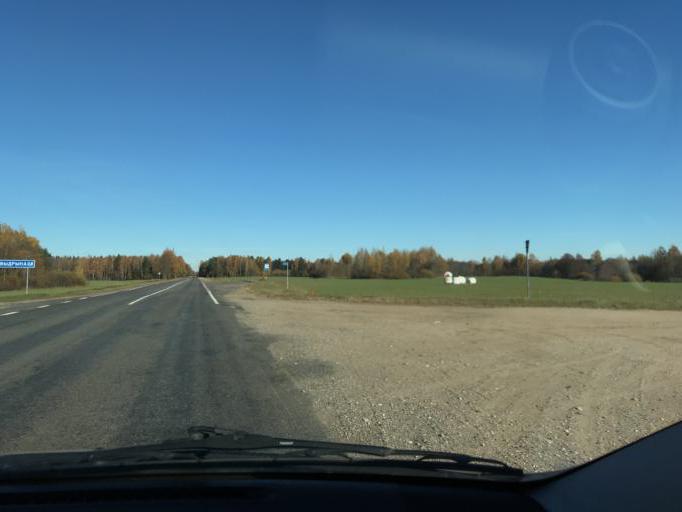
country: BY
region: Vitebsk
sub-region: Ushatski Rayon
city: Ushachy
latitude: 55.0860
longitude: 28.7560
